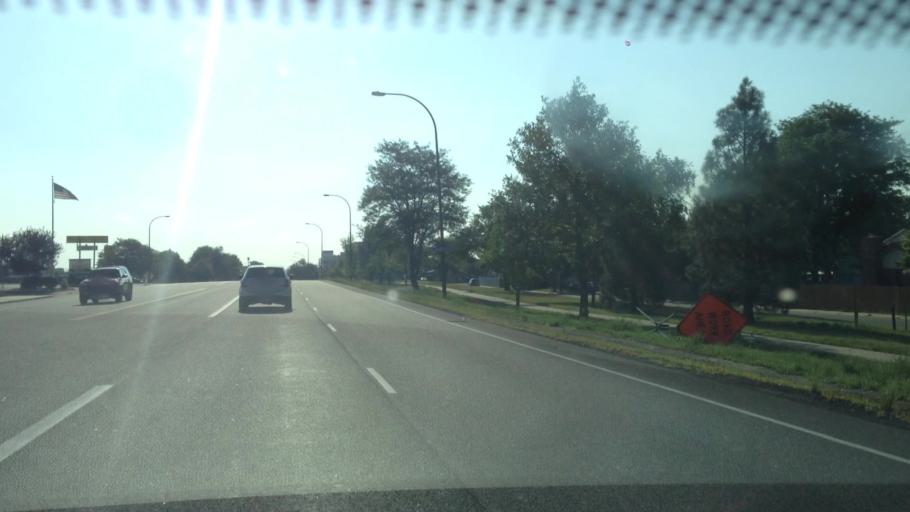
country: US
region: Colorado
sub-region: Jefferson County
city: Lakewood
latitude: 39.7110
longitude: -105.0694
